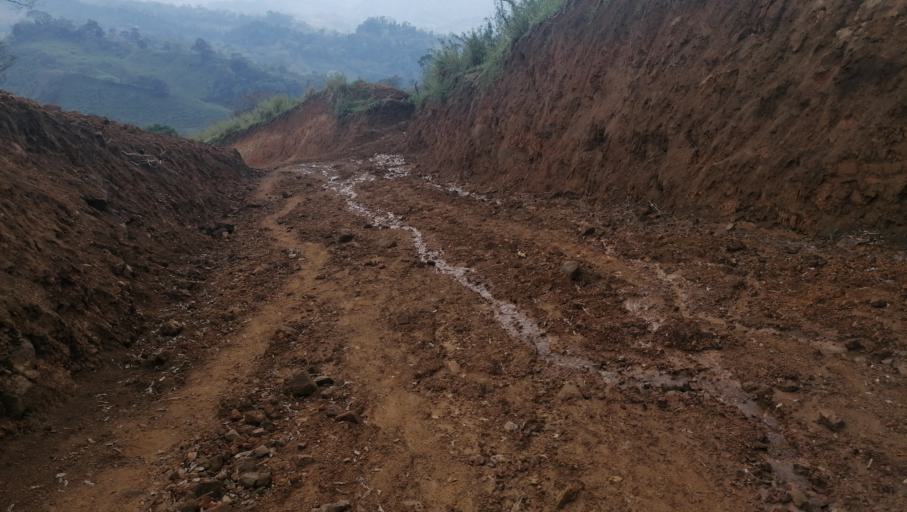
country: MX
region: Chiapas
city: Ostuacan
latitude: 17.3593
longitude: -93.3194
